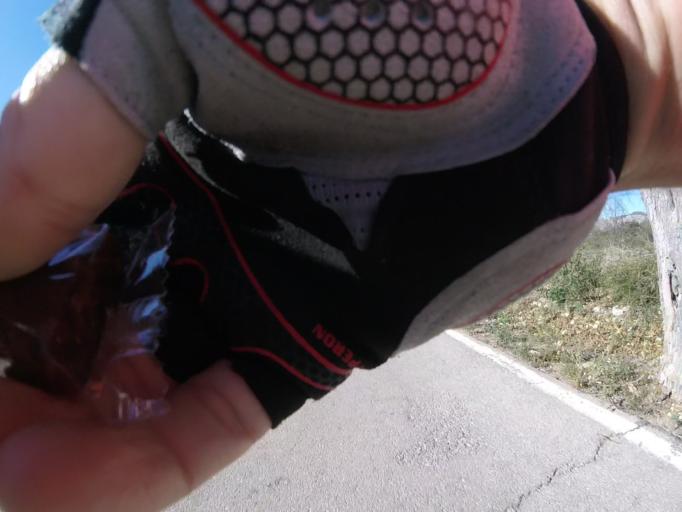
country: ES
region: Valencia
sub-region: Provincia de Castello
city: Chert/Xert
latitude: 40.4628
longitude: 0.1640
